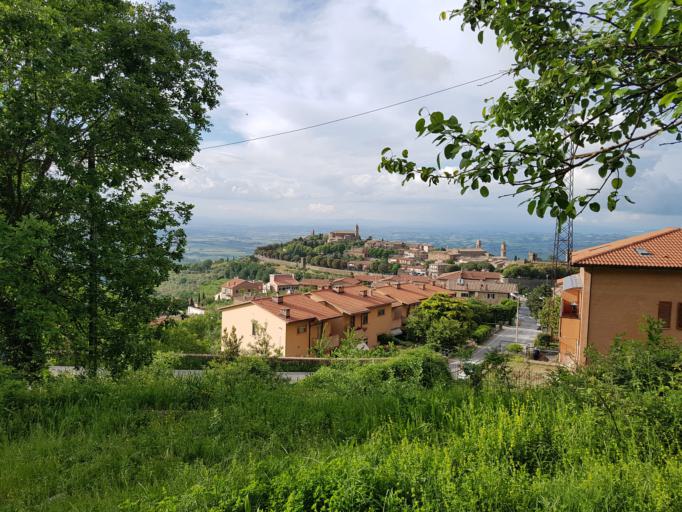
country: IT
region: Tuscany
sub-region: Provincia di Siena
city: Montalcino
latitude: 43.0522
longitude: 11.4875
